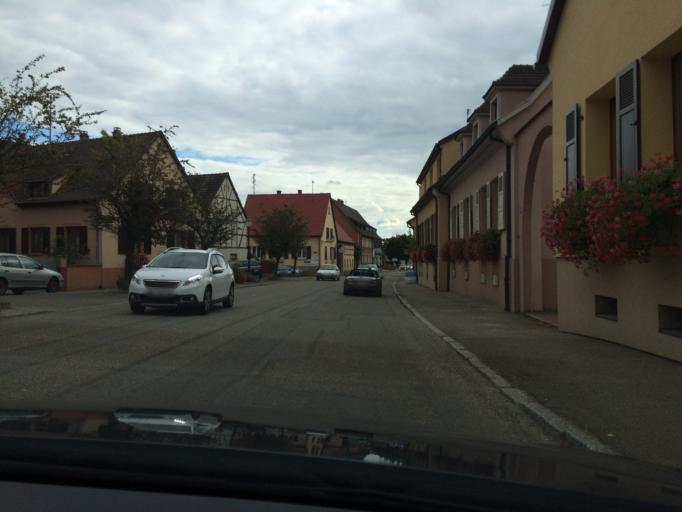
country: FR
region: Alsace
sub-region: Departement du Haut-Rhin
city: Bennwihr
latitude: 48.1444
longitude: 7.3244
